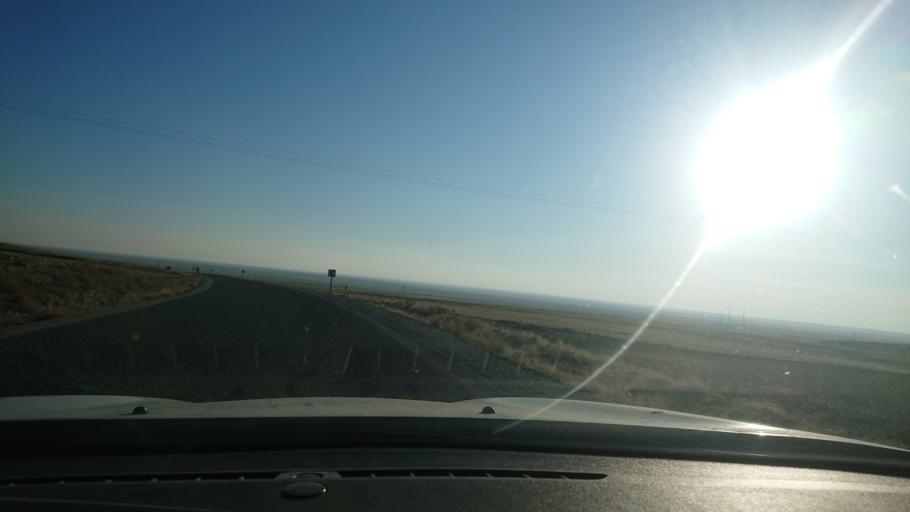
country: TR
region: Aksaray
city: Acipinar
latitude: 38.6843
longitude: 33.7357
